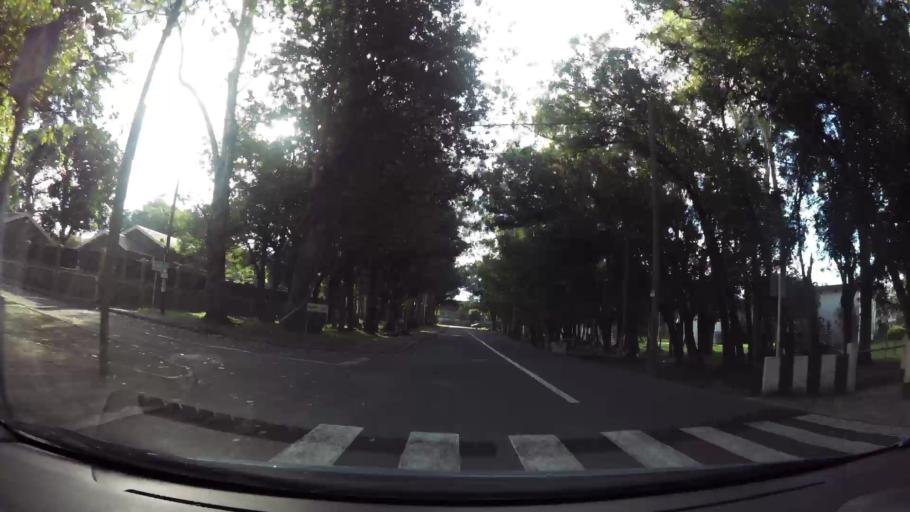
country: MU
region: Plaines Wilhems
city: Vacoas
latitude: -20.2954
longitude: 57.4974
